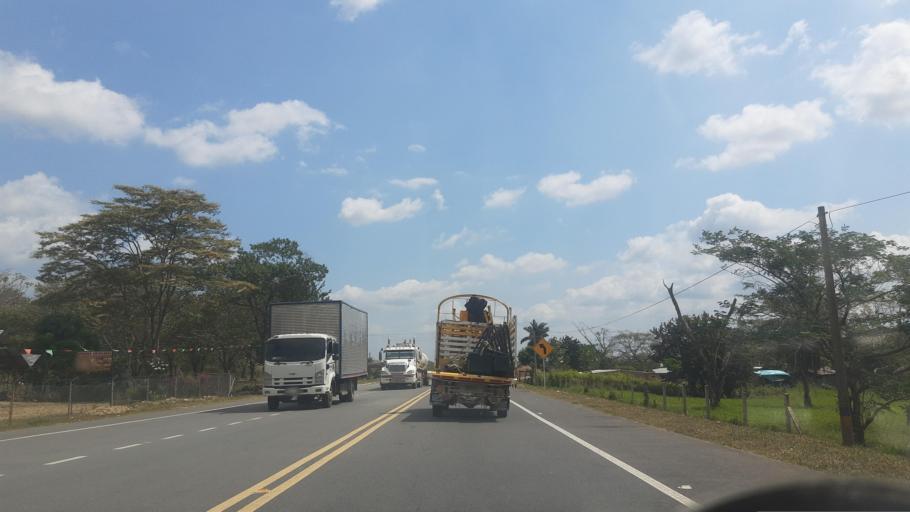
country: CO
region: Casanare
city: Tauramena
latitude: 5.0211
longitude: -72.6628
